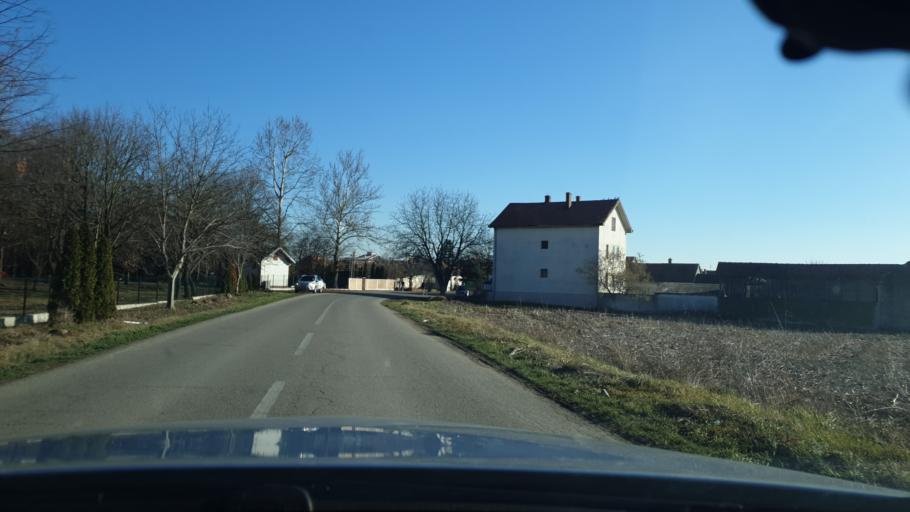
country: RS
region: Autonomna Pokrajina Vojvodina
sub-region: Sremski Okrug
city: Ruma
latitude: 45.0197
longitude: 19.8160
